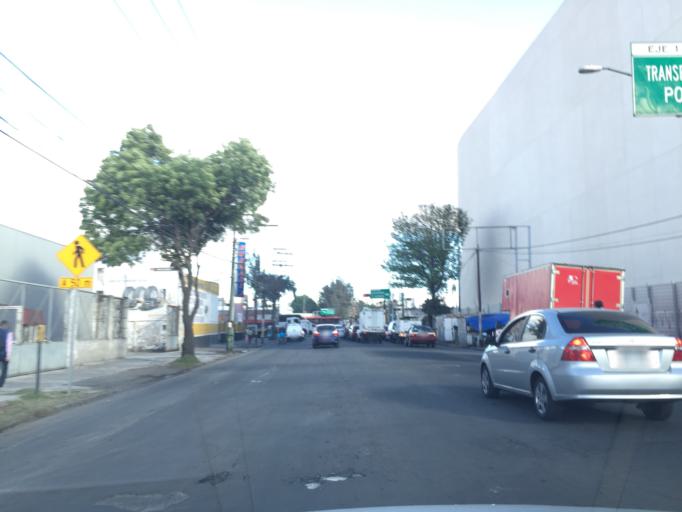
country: MX
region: Mexico
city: Colonia Lindavista
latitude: 19.4891
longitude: -99.1530
